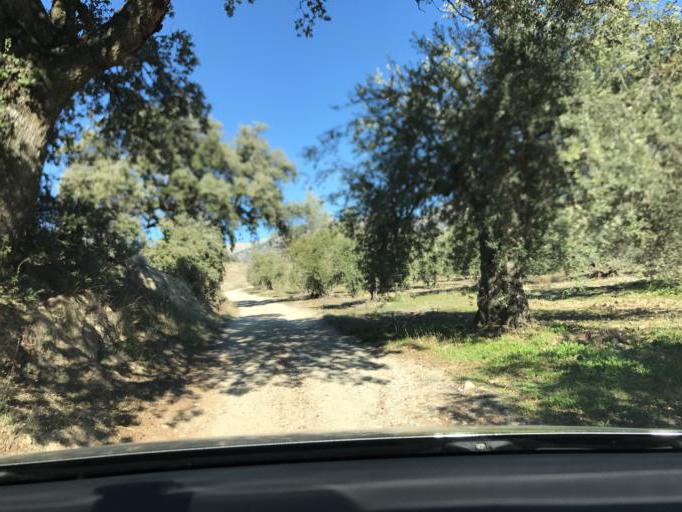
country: ES
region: Andalusia
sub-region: Provincia de Granada
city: Viznar
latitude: 37.2171
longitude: -3.5547
